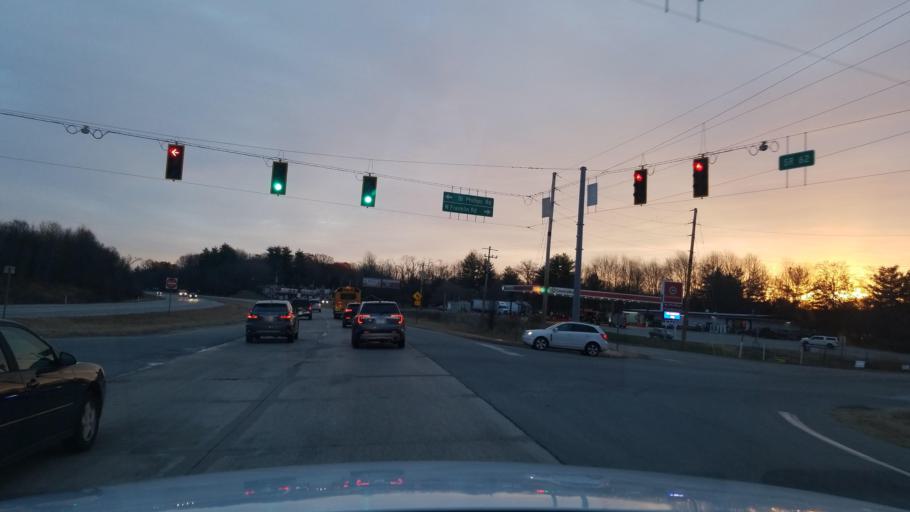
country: US
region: Indiana
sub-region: Vanderburgh County
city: Evansville
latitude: 37.9423
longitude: -87.7191
